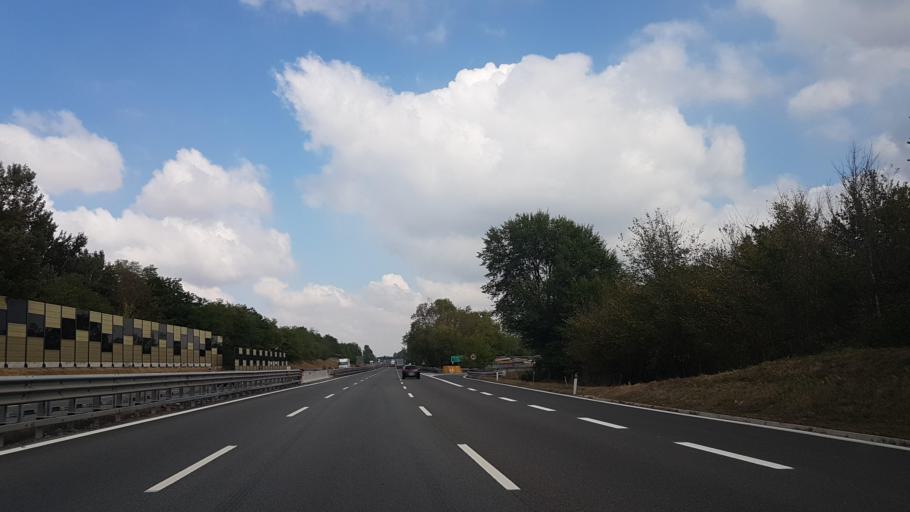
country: IT
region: Piedmont
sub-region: Provincia di Alessandria
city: Rocca Grimalda
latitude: 44.6787
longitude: 8.6587
